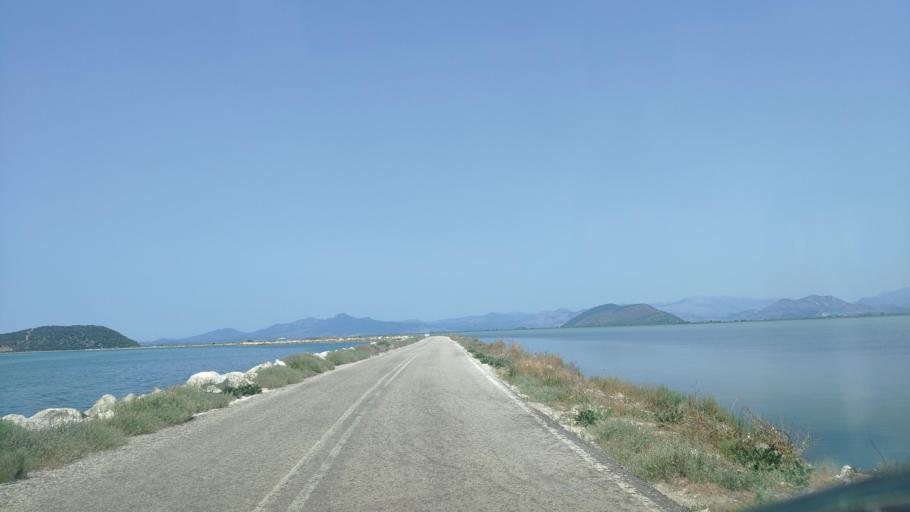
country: GR
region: Epirus
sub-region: Nomos Artas
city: Aneza
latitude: 39.0298
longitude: 20.8997
